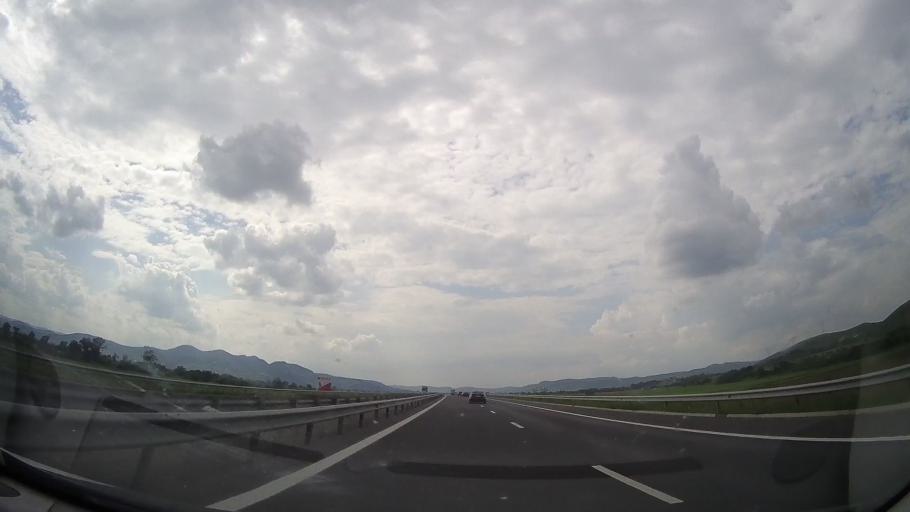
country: RO
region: Hunedoara
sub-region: Comuna Harau
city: Harau
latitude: 45.8874
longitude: 22.9763
